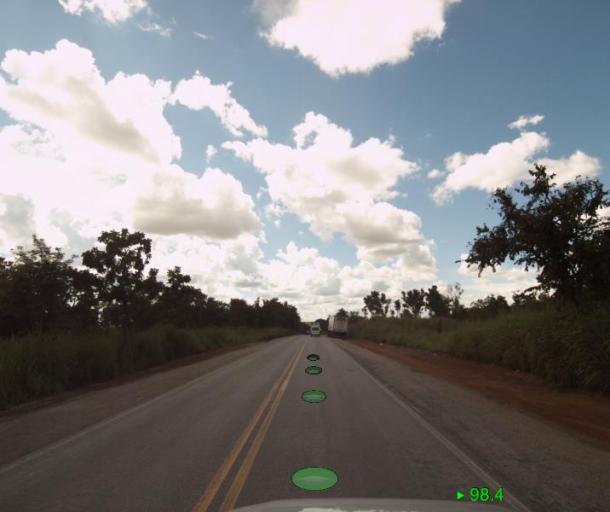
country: BR
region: Goias
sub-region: Porangatu
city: Porangatu
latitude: -13.6387
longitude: -49.0408
